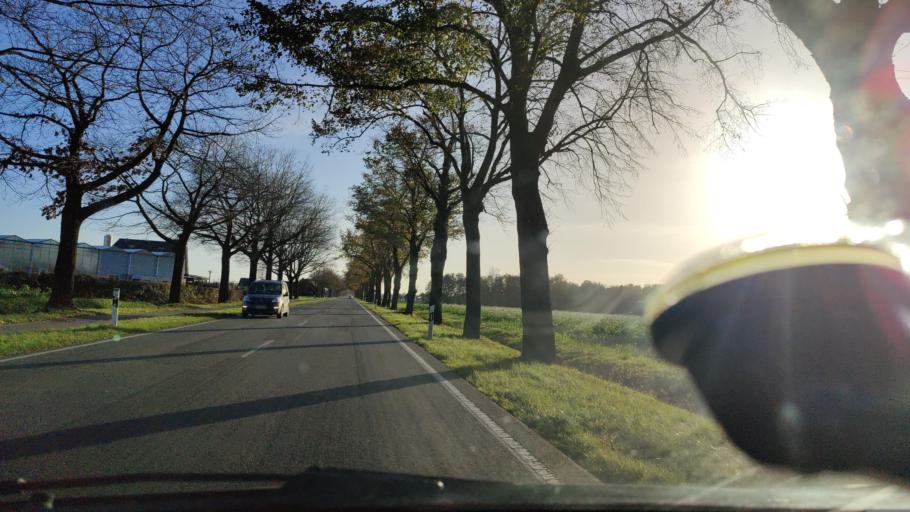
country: DE
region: North Rhine-Westphalia
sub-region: Regierungsbezirk Dusseldorf
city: Kevelaer
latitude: 51.5612
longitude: 6.2440
